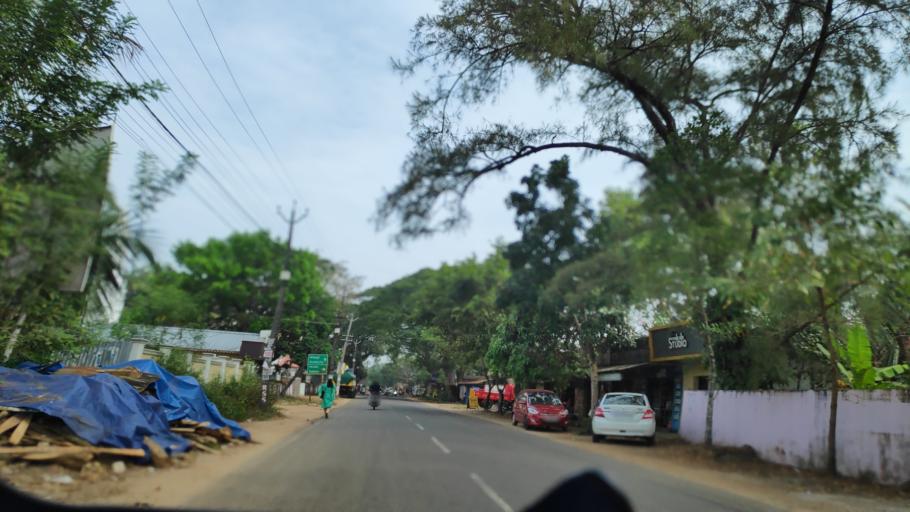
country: IN
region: Kerala
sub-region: Kottayam
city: Vaikam
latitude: 9.7504
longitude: 76.3632
